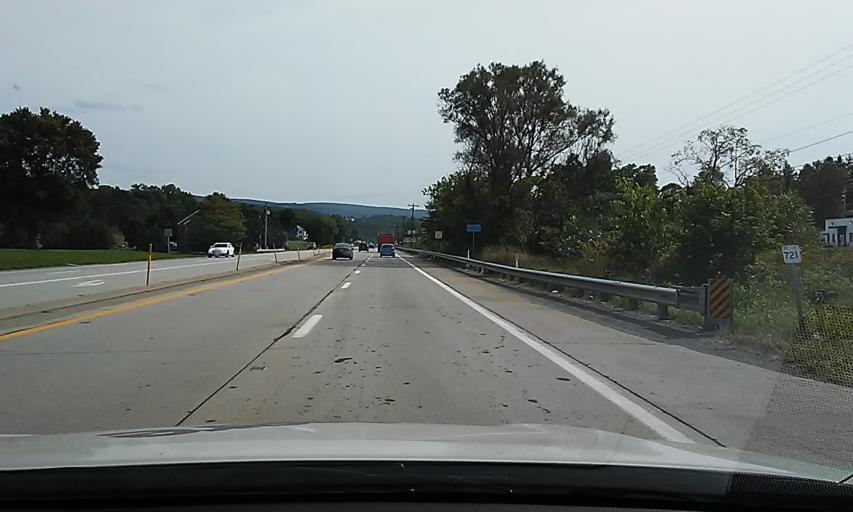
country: US
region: Pennsylvania
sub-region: Westmoreland County
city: Scottdale
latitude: 40.0676
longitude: -79.5646
